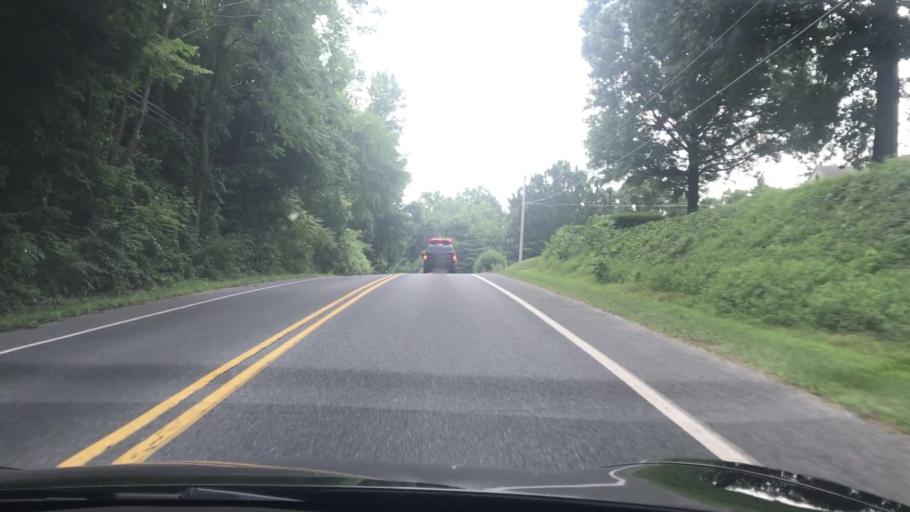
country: US
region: Pennsylvania
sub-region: York County
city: Valley Green
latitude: 40.1124
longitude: -76.7722
